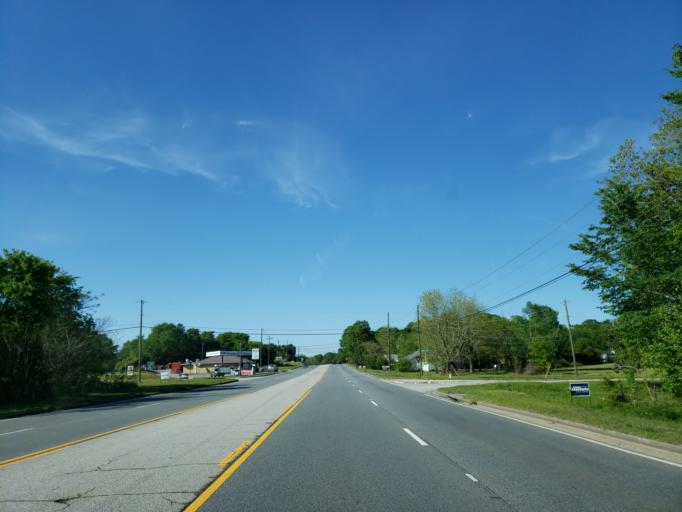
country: US
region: Georgia
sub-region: Polk County
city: Cedartown
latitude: 33.9703
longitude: -85.2596
